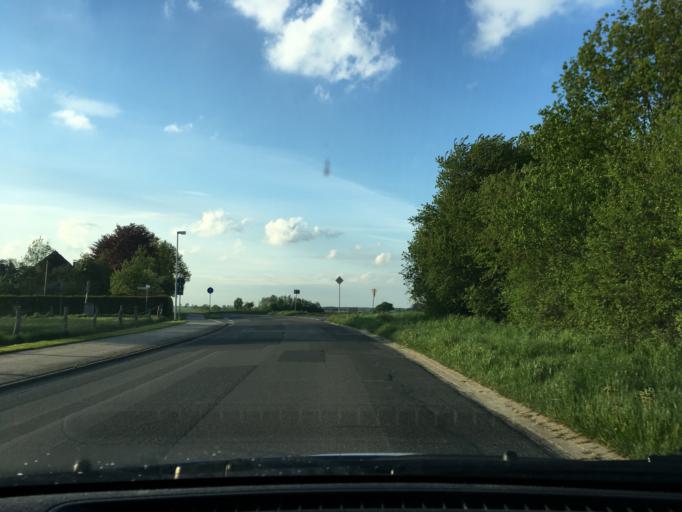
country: DE
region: Lower Saxony
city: Bergen
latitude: 52.8282
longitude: 9.9707
